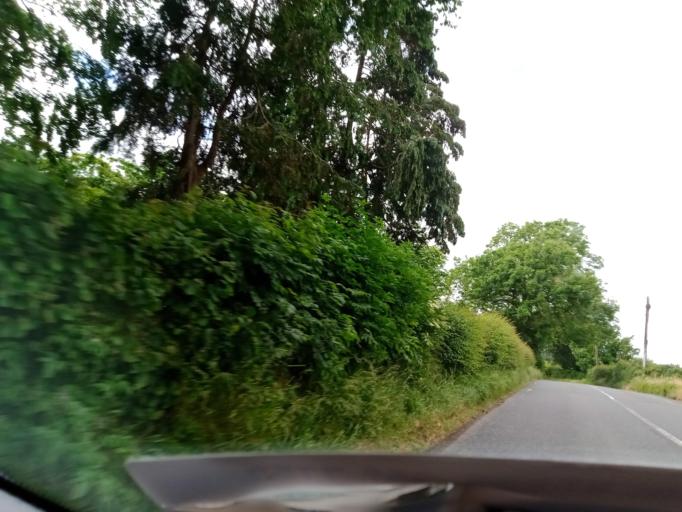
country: IE
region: Leinster
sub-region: Kilkenny
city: Thomastown
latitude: 52.4852
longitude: -7.2450
